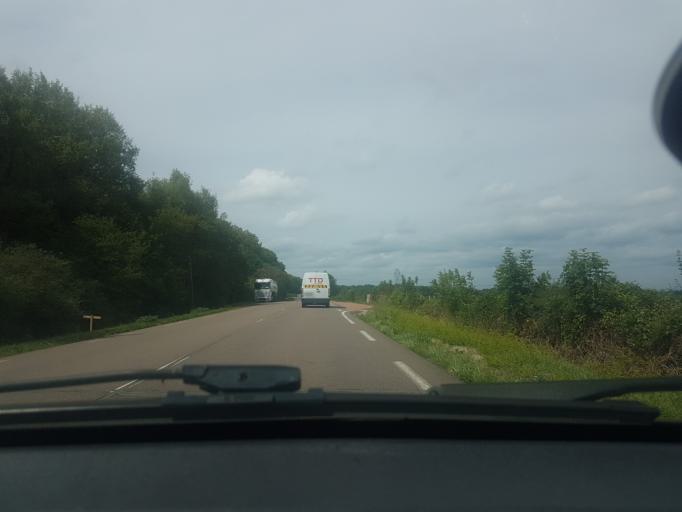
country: FR
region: Bourgogne
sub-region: Departement de la Cote-d'Or
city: Nolay
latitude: 47.0378
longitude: 4.6213
